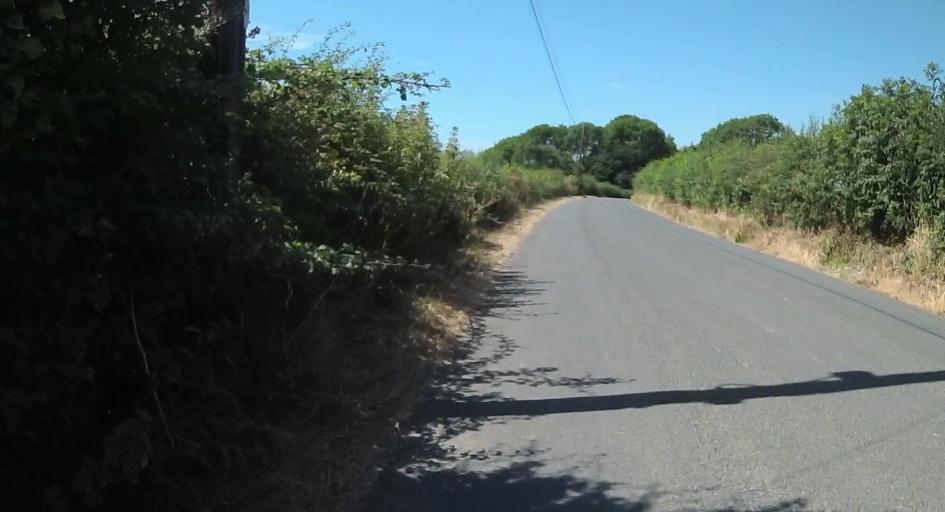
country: GB
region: England
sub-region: Dorset
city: Wareham
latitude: 50.6324
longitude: -2.1007
